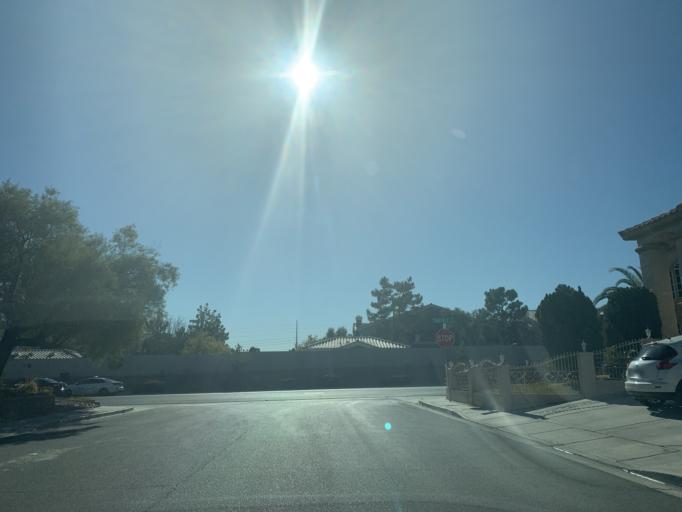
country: US
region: Nevada
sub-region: Clark County
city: Summerlin South
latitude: 36.1171
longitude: -115.2912
